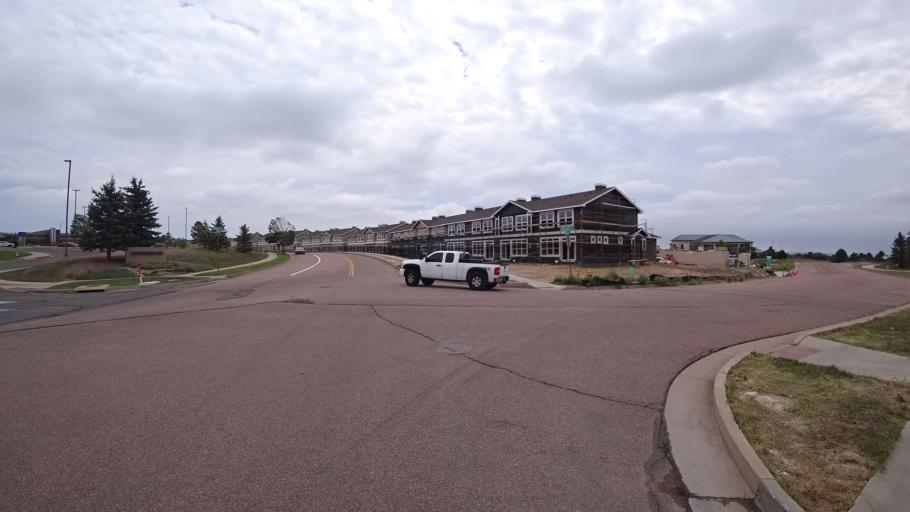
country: US
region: Colorado
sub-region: El Paso County
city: Gleneagle
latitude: 39.0126
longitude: -104.8166
